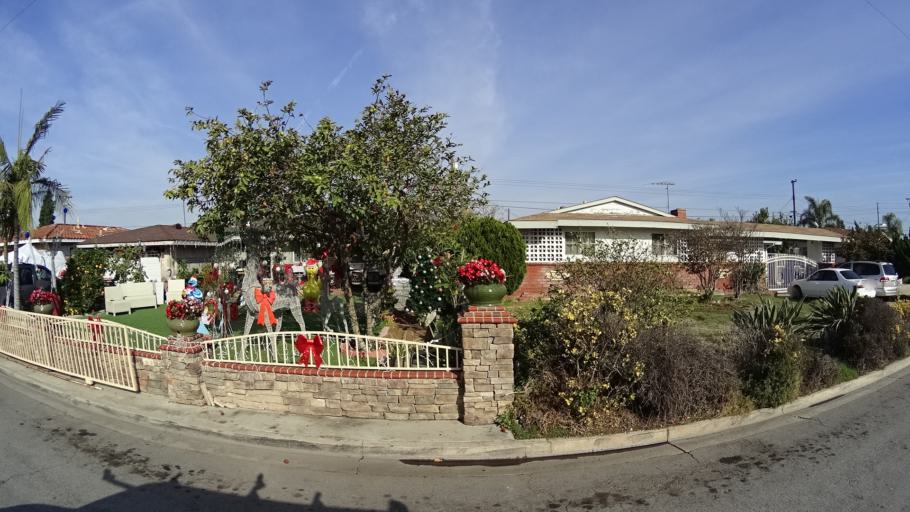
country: US
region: California
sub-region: Orange County
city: Garden Grove
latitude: 33.7910
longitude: -117.8989
